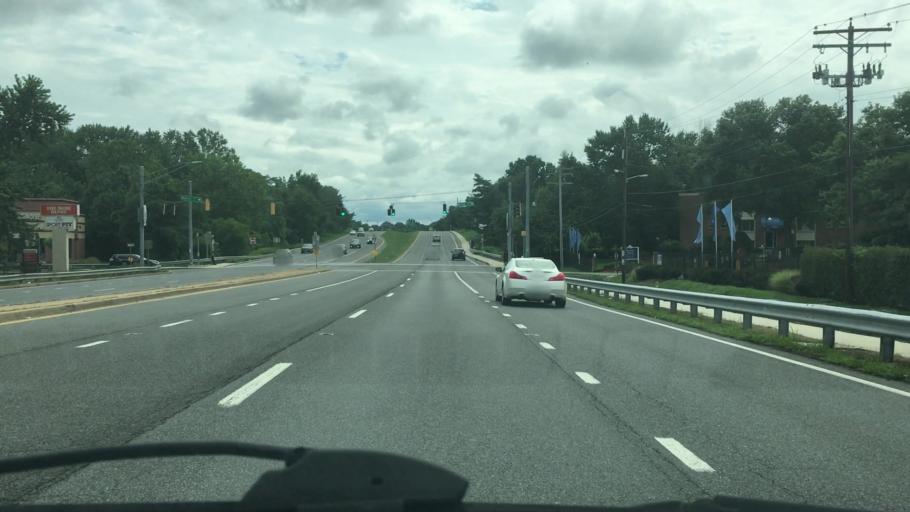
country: US
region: Maryland
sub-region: Prince George's County
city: Laurel
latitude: 39.0942
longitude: -76.8430
